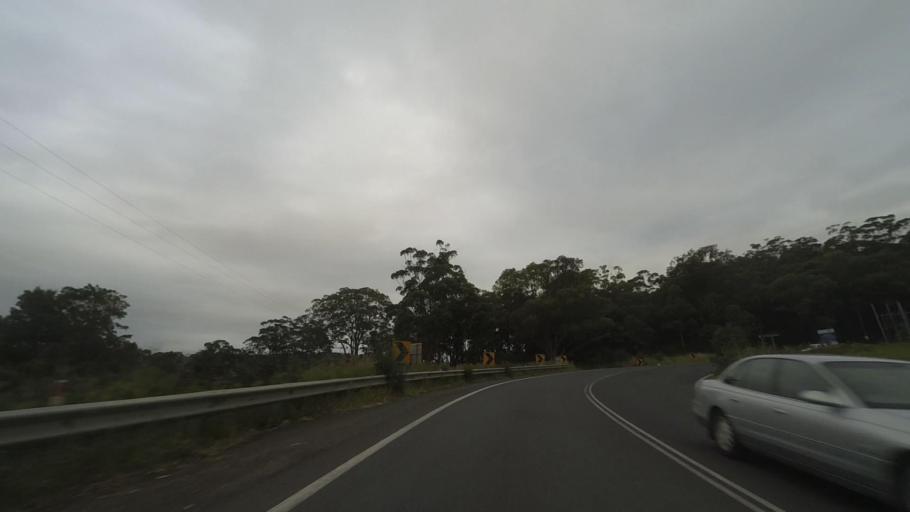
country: AU
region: New South Wales
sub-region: Kiama
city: Gerringong
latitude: -34.7400
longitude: 150.7649
